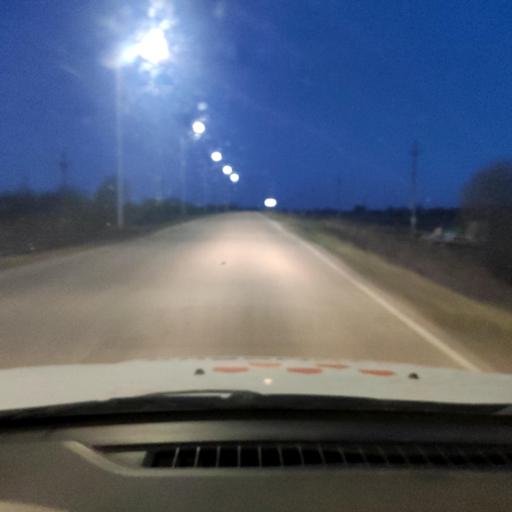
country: RU
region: Bashkortostan
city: Ulukulevo
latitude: 54.5645
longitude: 56.3393
